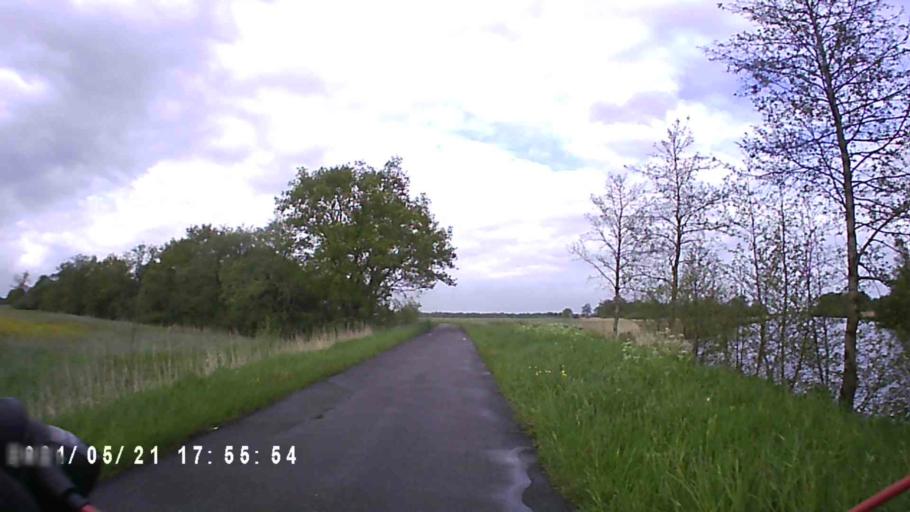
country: NL
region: Groningen
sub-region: Gemeente Leek
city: Leek
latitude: 53.1782
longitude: 6.4074
